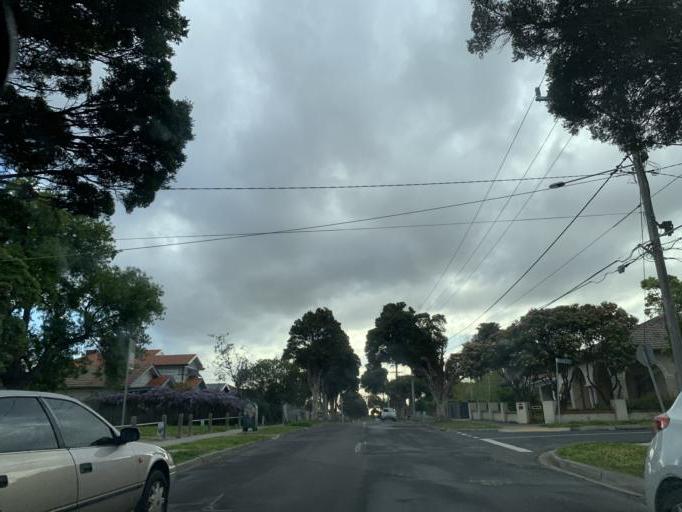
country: AU
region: Victoria
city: Thornbury
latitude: -37.7486
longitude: 144.9876
